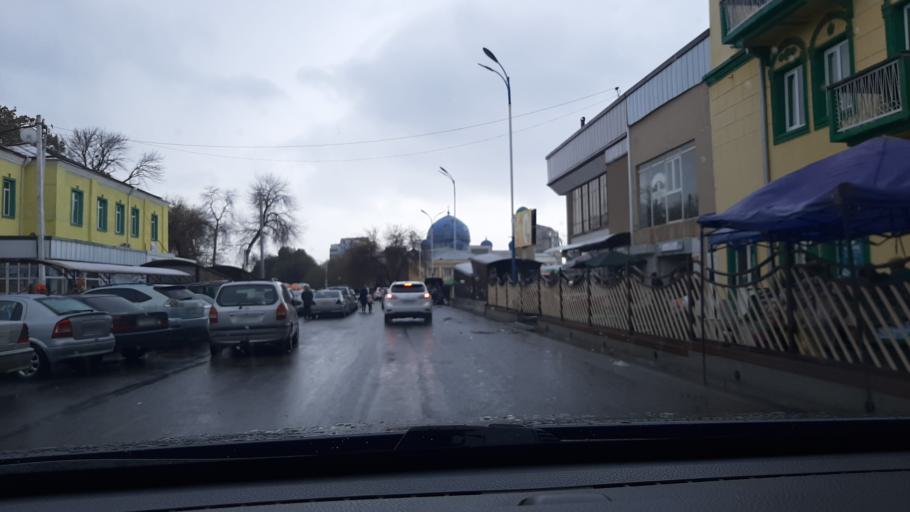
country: TJ
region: Viloyati Sughd
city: Khujand
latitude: 40.2785
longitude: 69.6328
